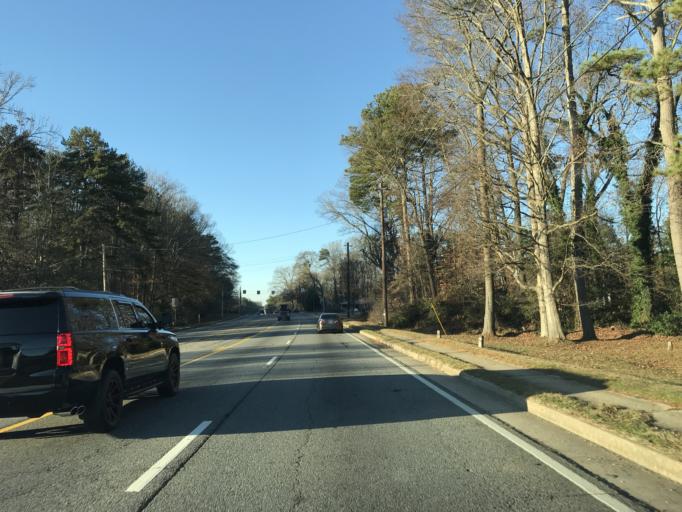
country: US
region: Georgia
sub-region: DeKalb County
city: Clarkston
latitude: 33.8361
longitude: -84.2406
